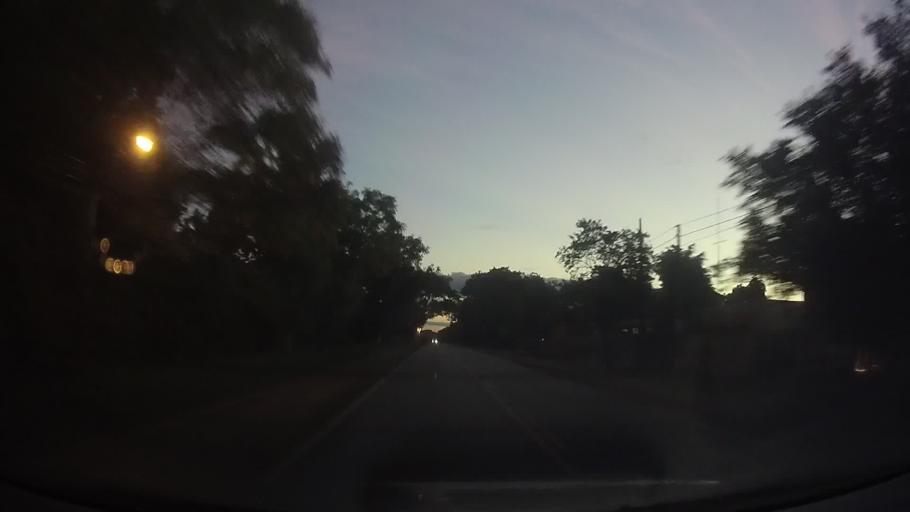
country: PY
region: Central
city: Itaugua
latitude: -25.4052
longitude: -57.3590
